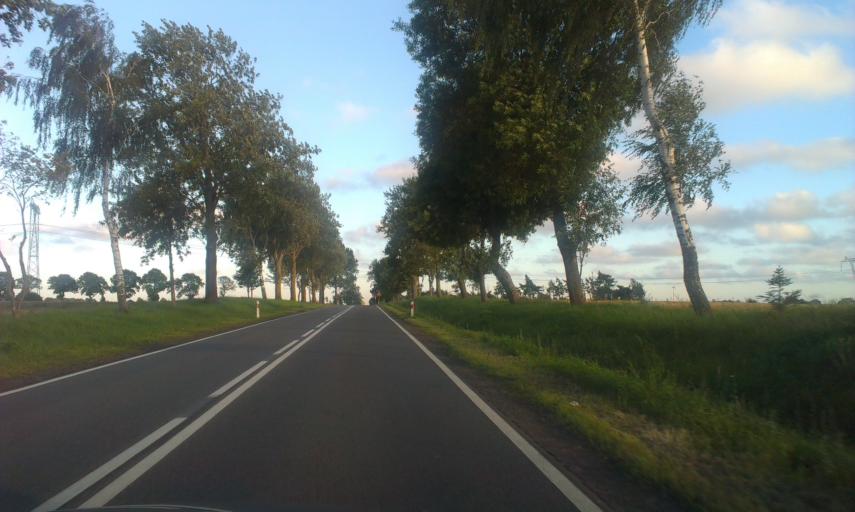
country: PL
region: West Pomeranian Voivodeship
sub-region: Powiat slawienski
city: Slawno
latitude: 54.3359
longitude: 16.5479
